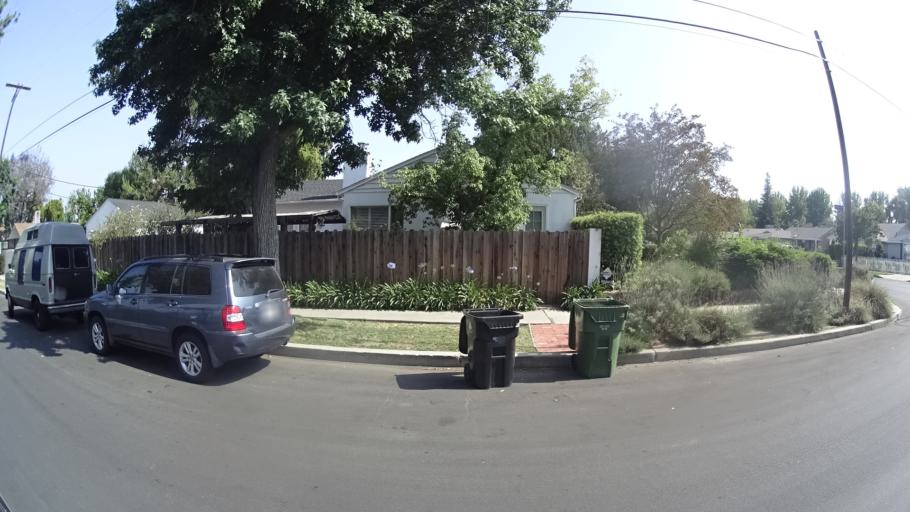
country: US
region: California
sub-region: Los Angeles County
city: Van Nuys
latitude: 34.1711
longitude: -118.4626
